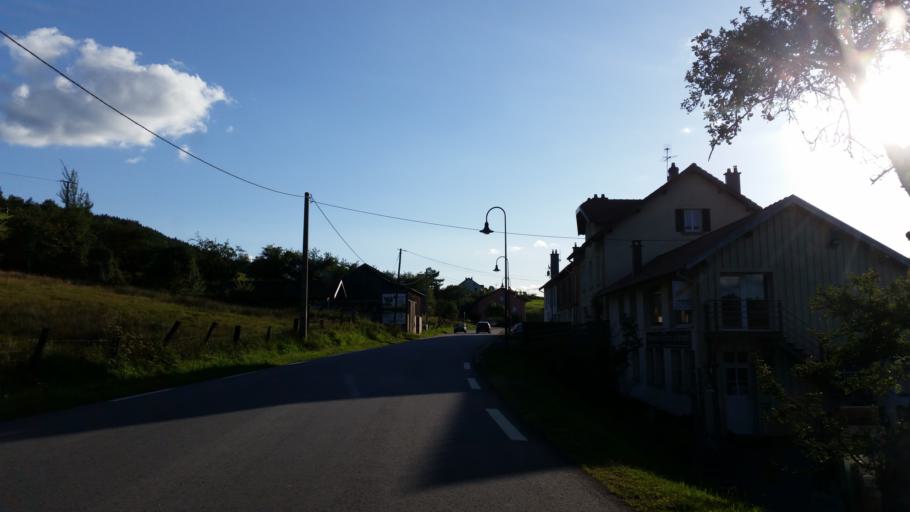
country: FR
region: Lorraine
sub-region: Departement des Vosges
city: Le Tholy
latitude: 48.0582
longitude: 6.7145
